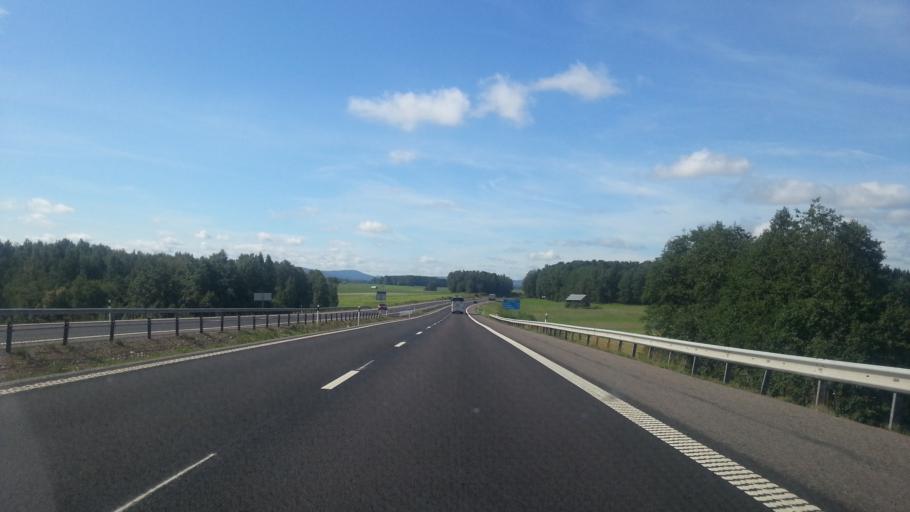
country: SE
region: Dalarna
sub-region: Borlange Kommun
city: Ornas
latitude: 60.5008
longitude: 15.5155
